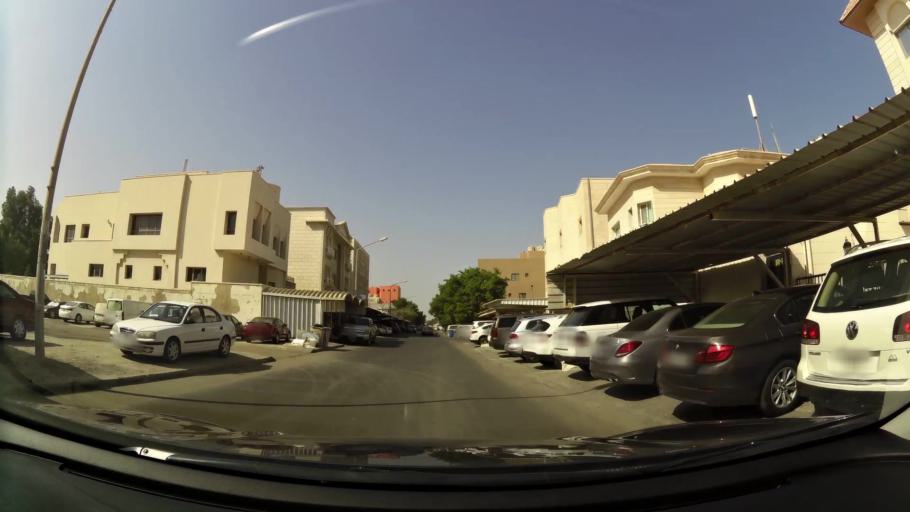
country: KW
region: Muhafazat Hawalli
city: Salwa
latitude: 29.2789
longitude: 48.0806
